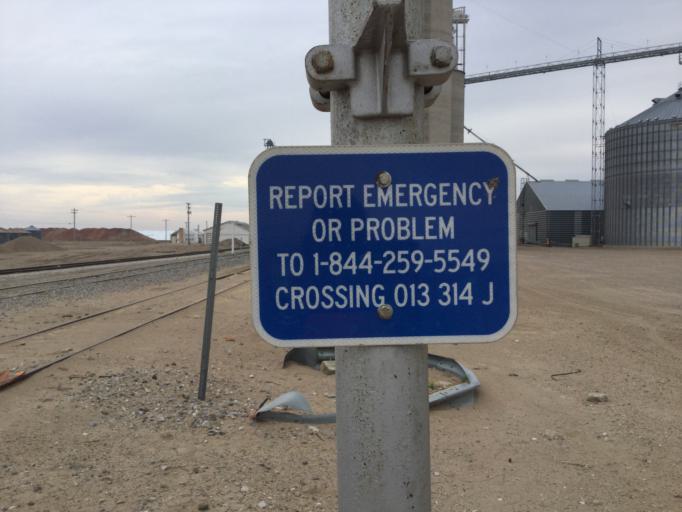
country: US
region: Kansas
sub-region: Stanton County
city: Johnson
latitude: 37.5622
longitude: -101.5629
